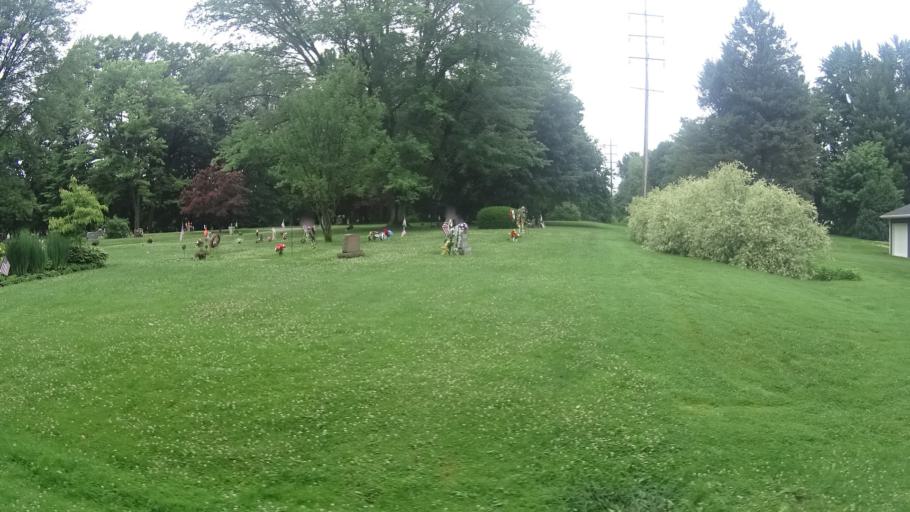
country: US
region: Ohio
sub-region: Erie County
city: Huron
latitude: 41.3181
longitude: -82.4943
